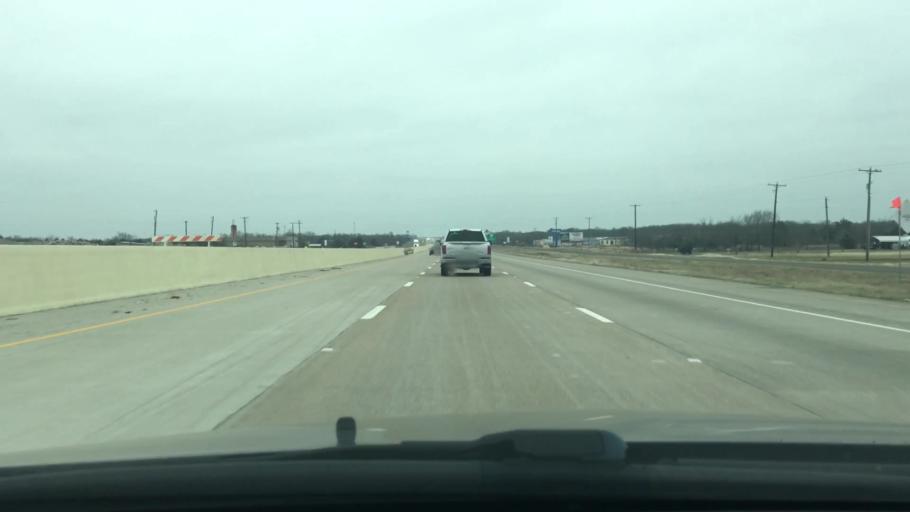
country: US
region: Texas
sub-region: Navarro County
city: Corsicana
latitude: 32.0281
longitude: -96.4420
